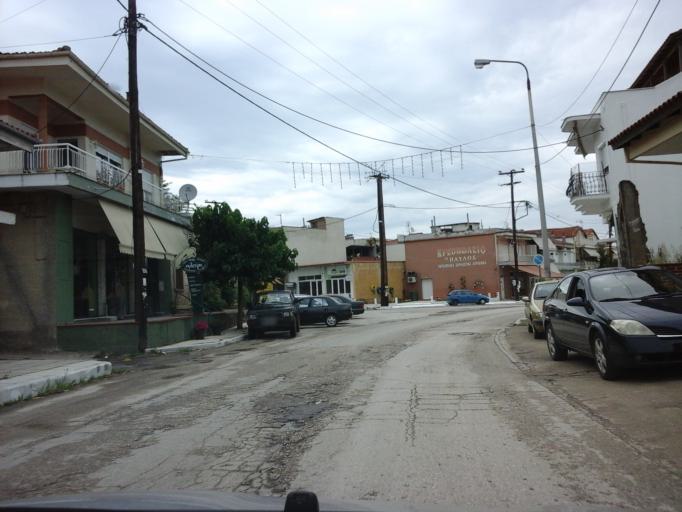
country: GR
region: East Macedonia and Thrace
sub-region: Nomos Evrou
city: Soufli
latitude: 41.1895
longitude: 26.3011
